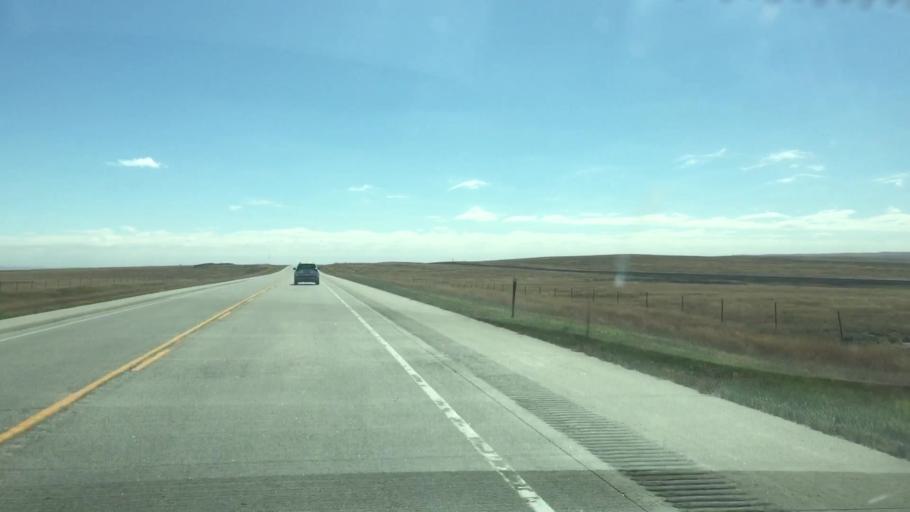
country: US
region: Colorado
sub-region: Lincoln County
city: Hugo
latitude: 39.1791
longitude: -103.5443
